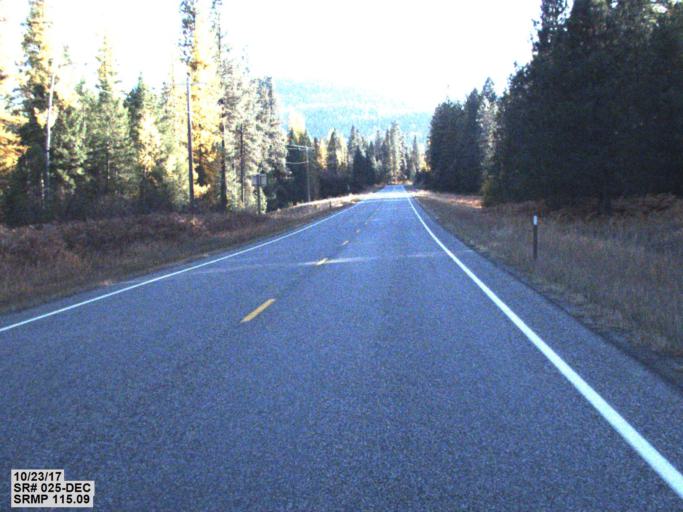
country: CA
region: British Columbia
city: Rossland
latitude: 48.9360
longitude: -117.7725
